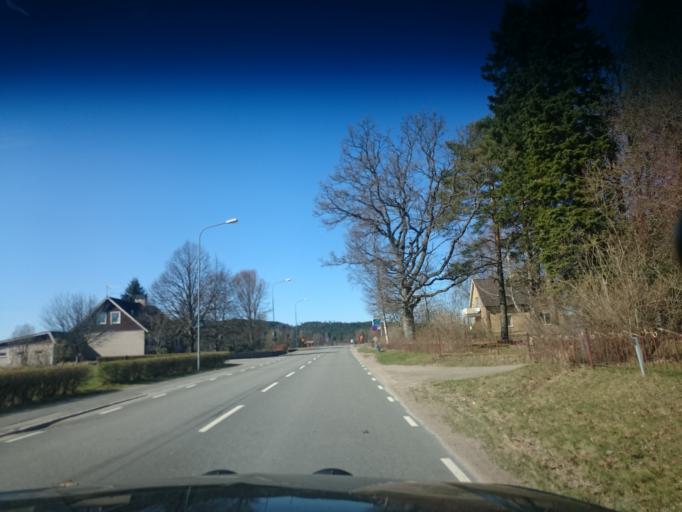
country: SE
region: Joenkoeping
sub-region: Vetlanda Kommun
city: Landsbro
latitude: 57.2050
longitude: 14.9479
